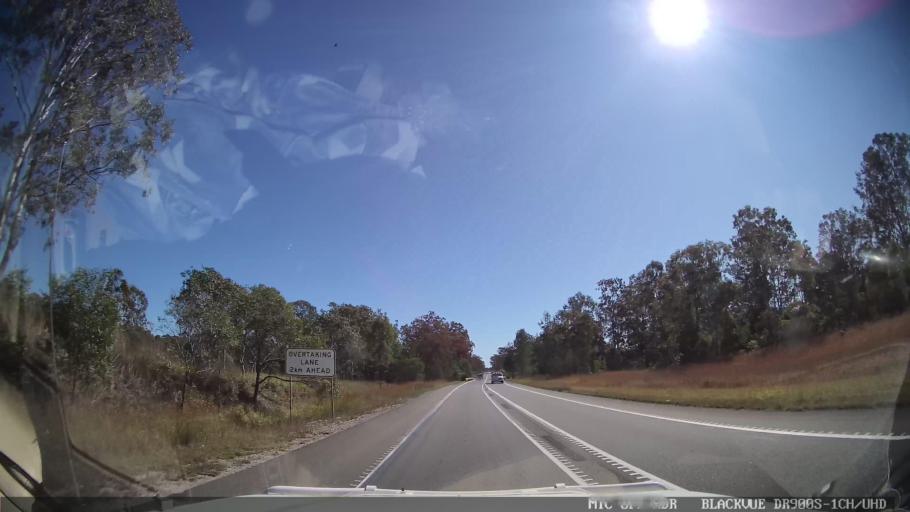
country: AU
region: Queensland
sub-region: Gympie Regional Council
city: Gympie
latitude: -26.0437
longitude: 152.5722
